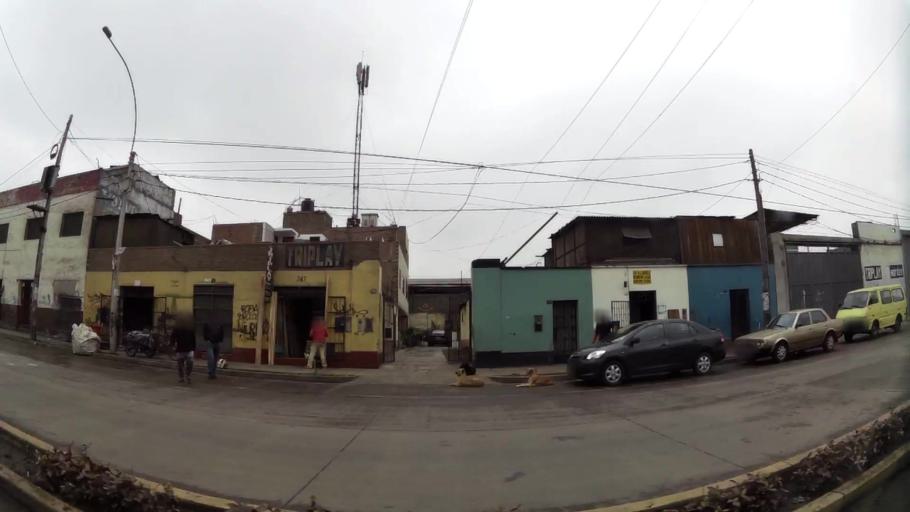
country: PE
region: Lima
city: Lima
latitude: -12.0662
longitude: -77.0214
